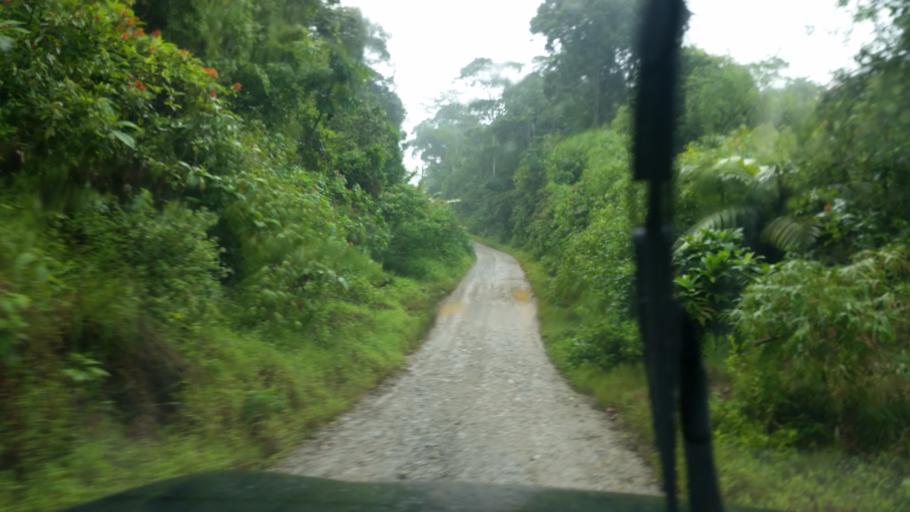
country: NI
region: Atlantico Norte (RAAN)
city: Bonanza
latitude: 14.0760
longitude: -84.6552
